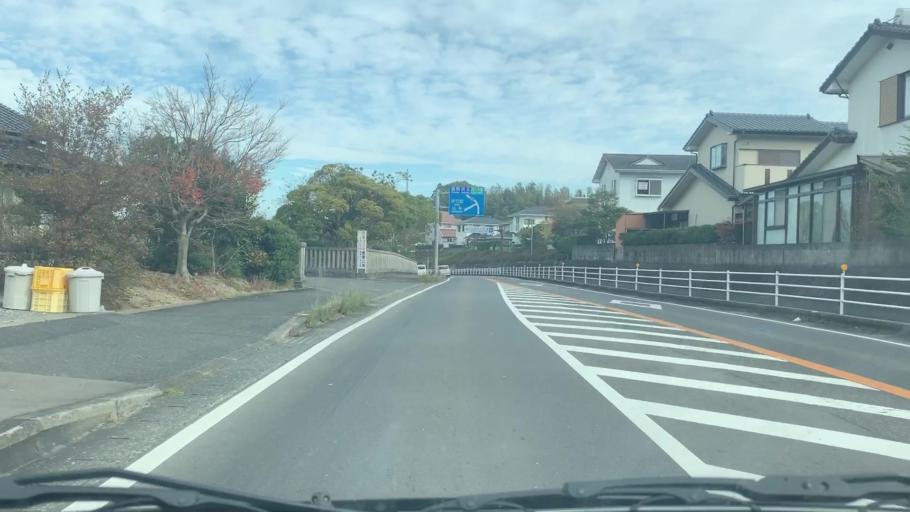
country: JP
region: Saga Prefecture
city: Karatsu
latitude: 33.3969
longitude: 129.9871
